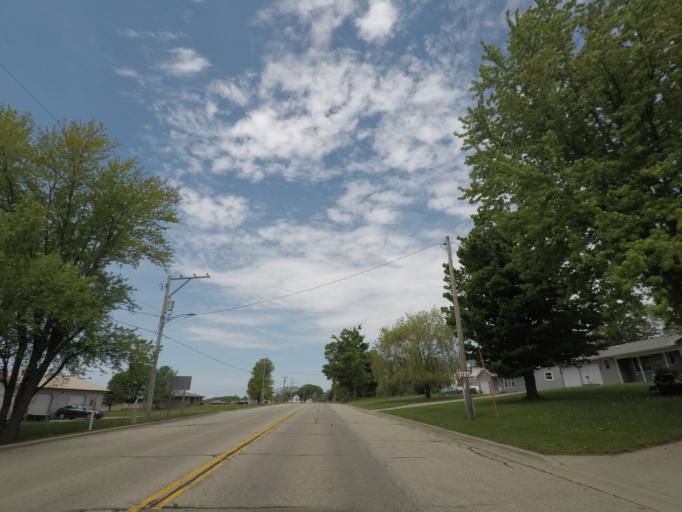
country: US
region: Wisconsin
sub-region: Rock County
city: Orfordville
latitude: 42.6336
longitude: -89.2655
